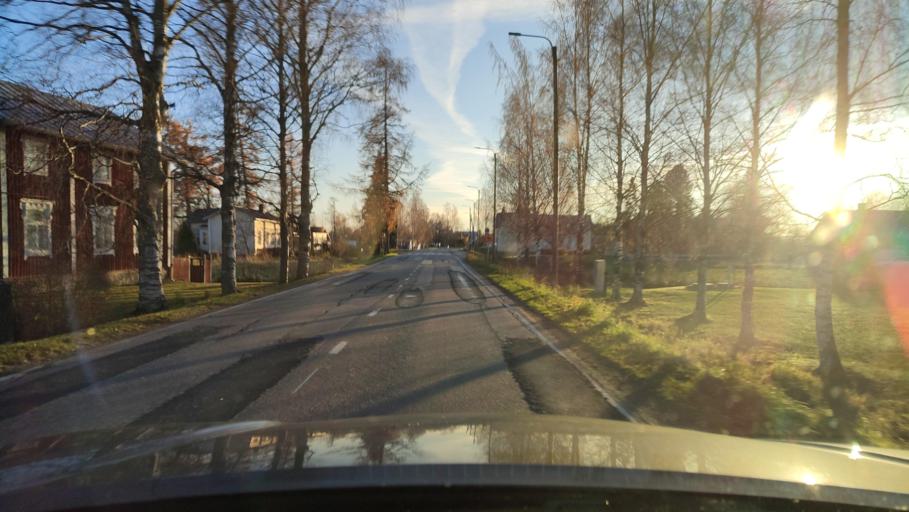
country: FI
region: Ostrobothnia
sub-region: Sydosterbotten
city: Naerpes
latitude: 62.6162
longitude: 21.4779
